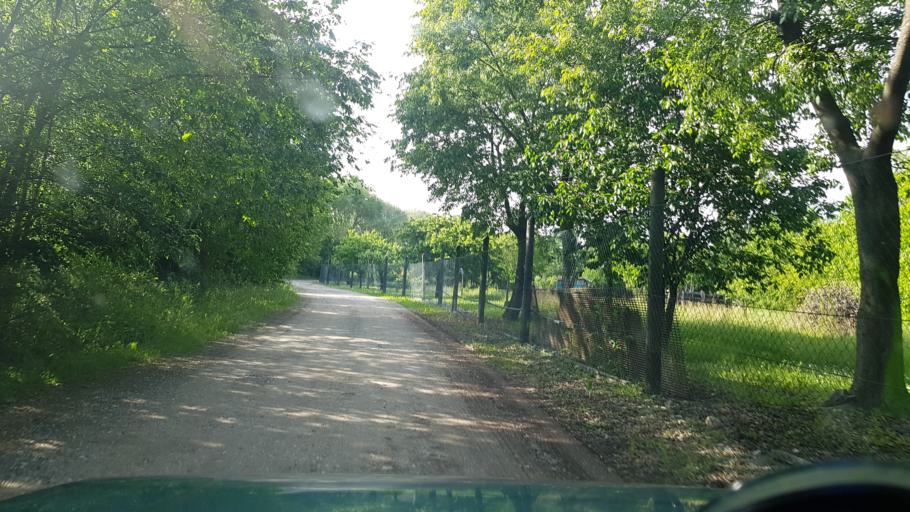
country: IT
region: Friuli Venezia Giulia
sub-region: Provincia di Gorizia
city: Romans d'Isonzo
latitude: 45.8836
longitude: 13.4588
